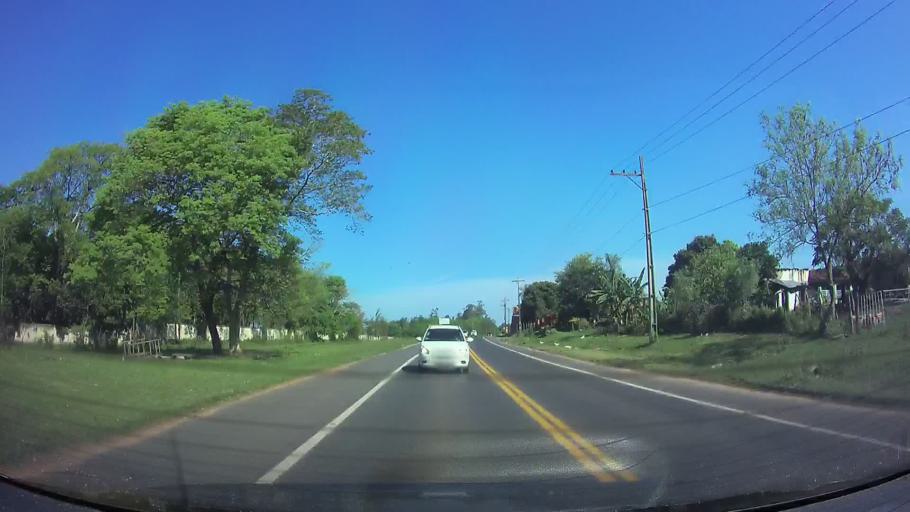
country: PY
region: Central
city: Itaugua
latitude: -25.3752
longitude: -57.3031
